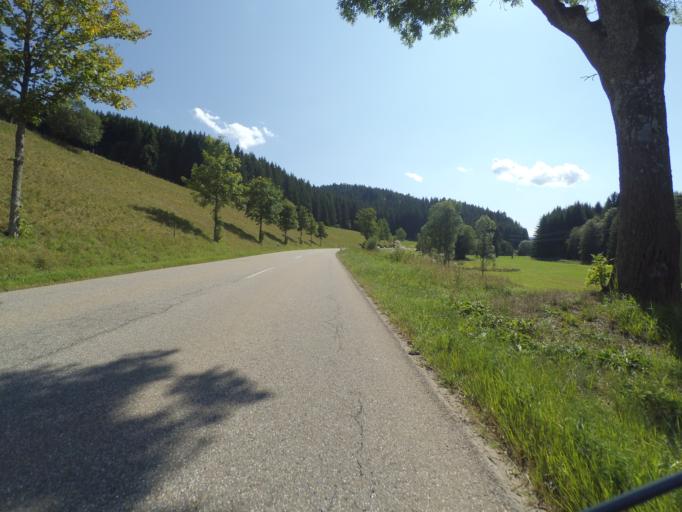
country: DE
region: Baden-Wuerttemberg
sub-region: Freiburg Region
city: Titisee-Neustadt
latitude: 47.9350
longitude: 8.1978
